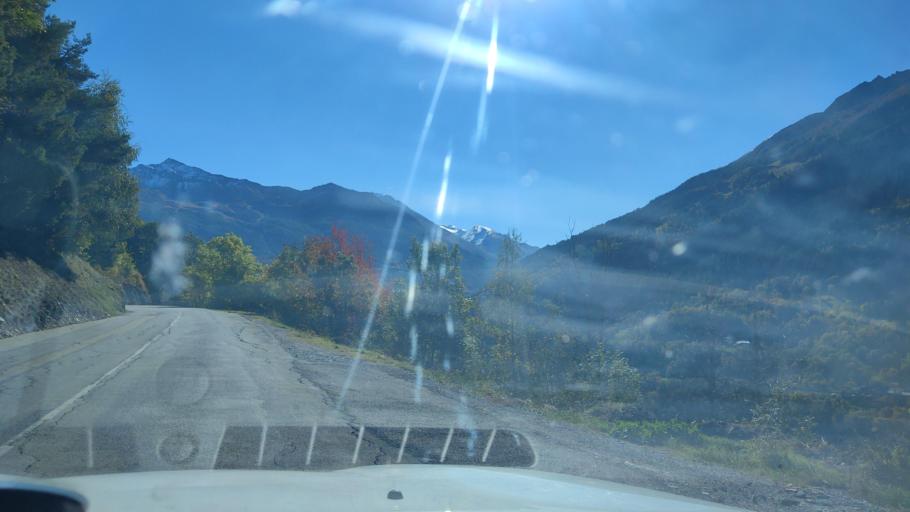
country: FR
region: Rhone-Alpes
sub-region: Departement de la Savoie
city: Seez
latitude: 45.6136
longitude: 6.8419
